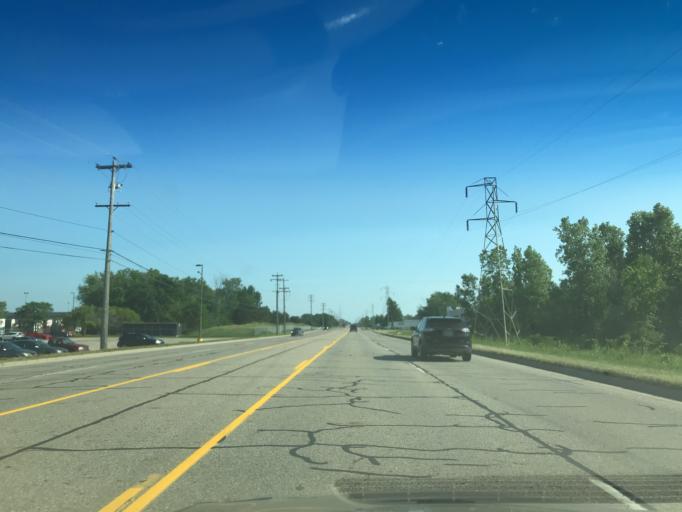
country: US
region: Michigan
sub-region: Eaton County
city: Waverly
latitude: 42.7062
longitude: -84.6424
